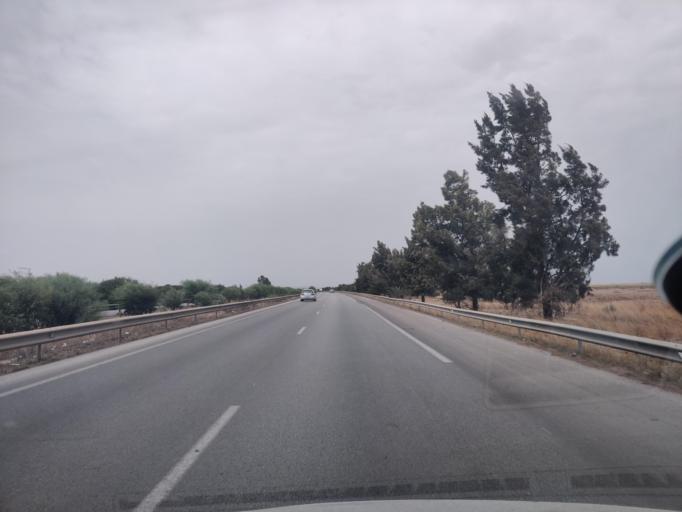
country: TN
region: Susah
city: Sidi Bou Ali
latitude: 36.0250
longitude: 10.4262
